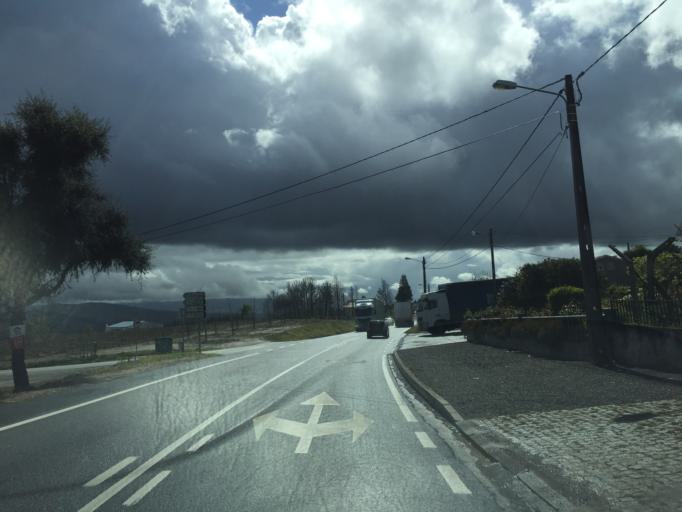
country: PT
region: Coimbra
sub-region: Oliveira do Hospital
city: Oliveira do Hospital
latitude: 40.3309
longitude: -7.8693
